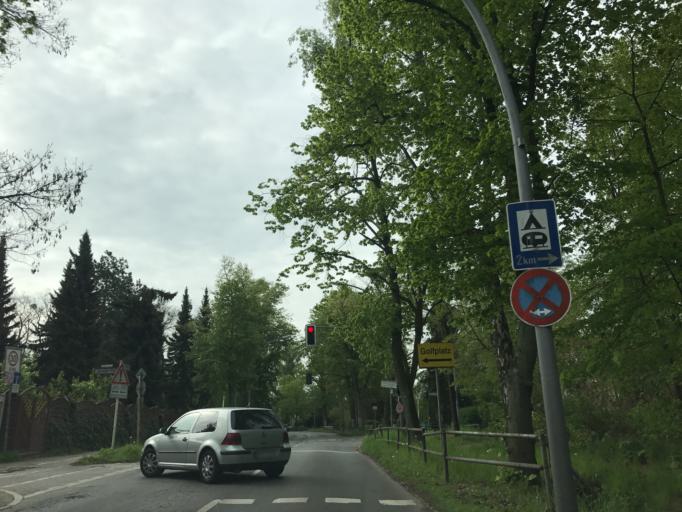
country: DE
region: Berlin
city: Kladow
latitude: 52.4646
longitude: 13.1298
